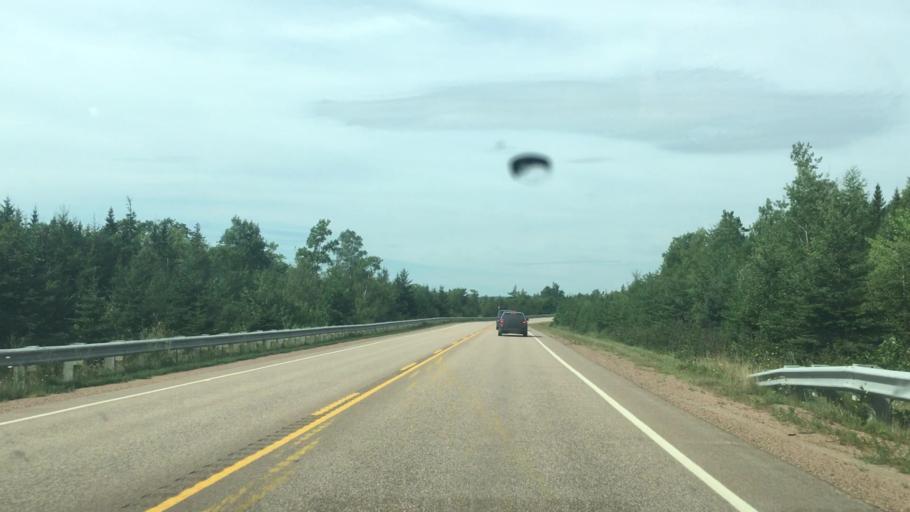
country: CA
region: Nova Scotia
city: Port Hawkesbury
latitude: 45.6044
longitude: -61.3114
